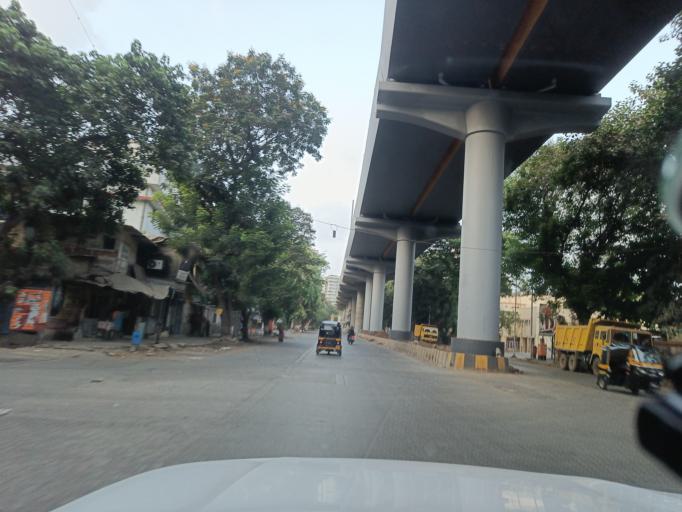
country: IN
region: Maharashtra
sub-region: Mumbai Suburban
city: Mumbai
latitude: 19.1244
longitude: 72.8306
